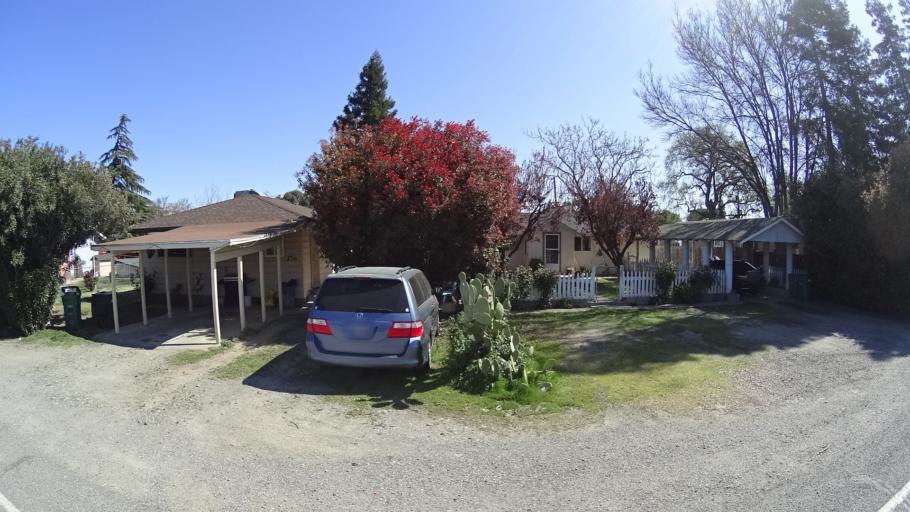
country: US
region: California
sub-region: Glenn County
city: Hamilton City
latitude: 39.7410
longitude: -122.0176
